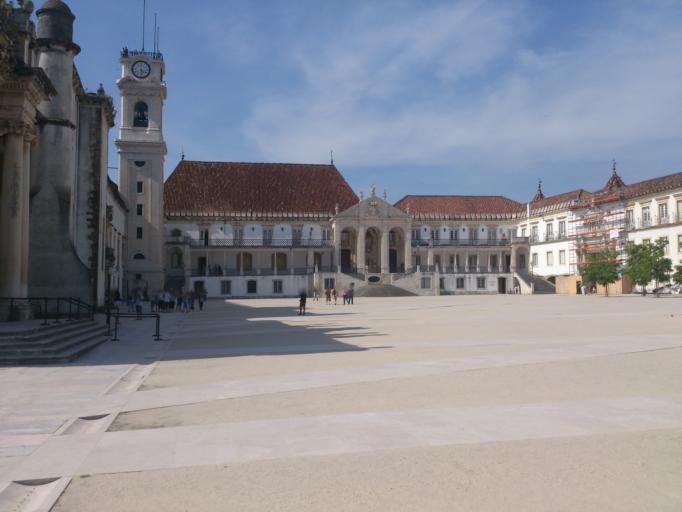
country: PT
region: Coimbra
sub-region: Coimbra
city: Coimbra
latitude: 40.2070
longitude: -8.4262
